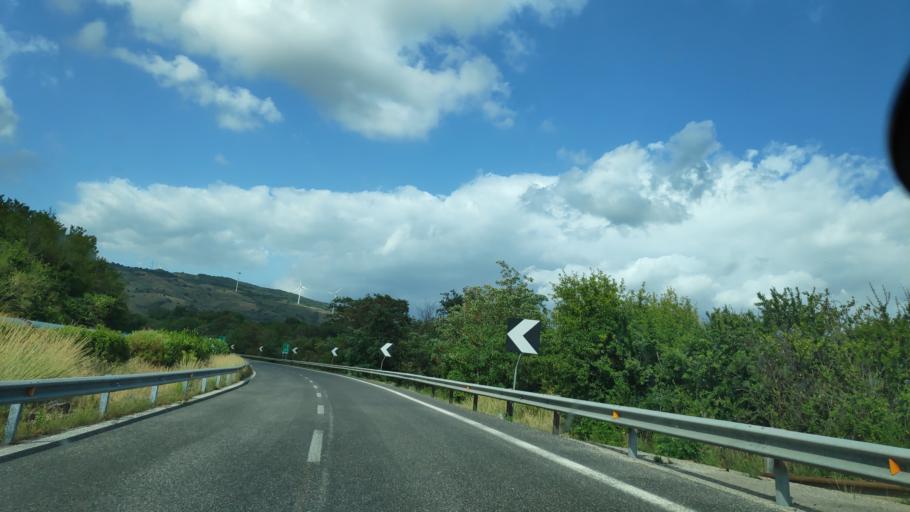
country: IT
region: Campania
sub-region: Provincia di Salerno
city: Serre
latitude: 40.6169
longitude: 15.1802
